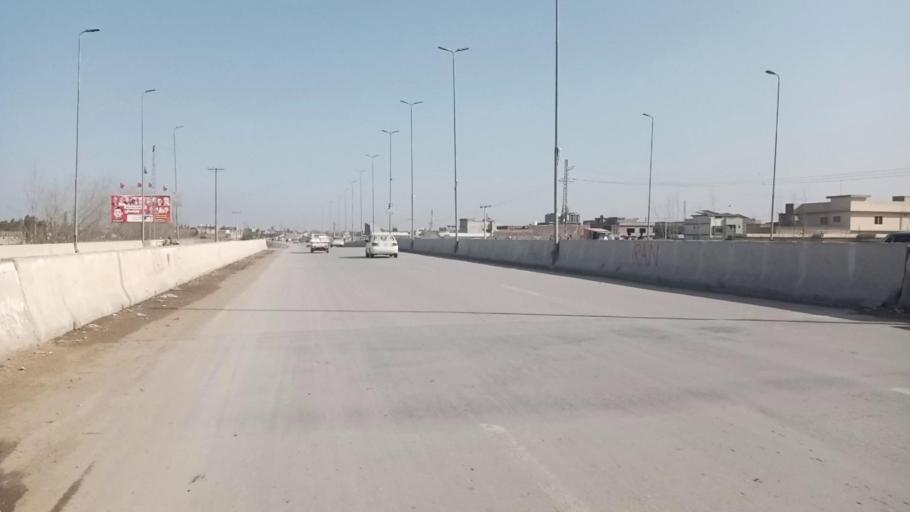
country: PK
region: Khyber Pakhtunkhwa
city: Peshawar
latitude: 34.0341
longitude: 71.5664
